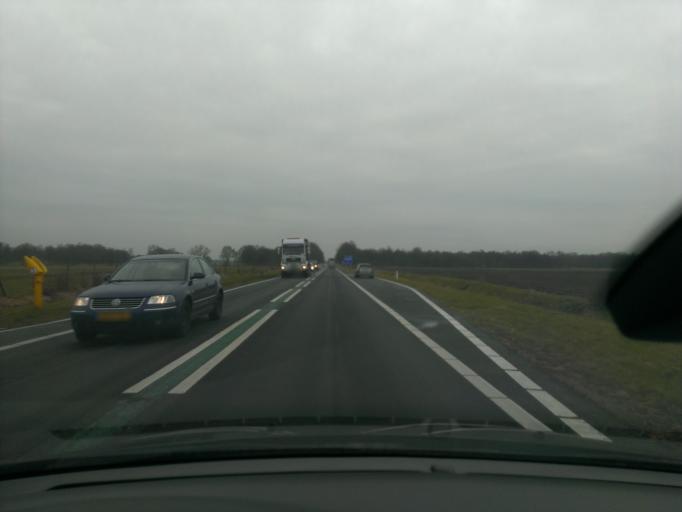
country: NL
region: Overijssel
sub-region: Gemeente Twenterand
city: Westerhaar-Vriezenveensewijk
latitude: 52.4416
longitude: 6.6289
